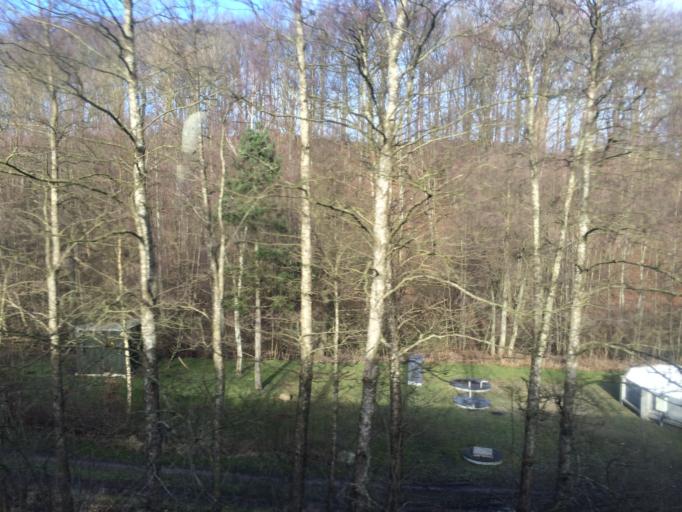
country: DK
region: South Denmark
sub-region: Vejle Kommune
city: Jelling
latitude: 55.7665
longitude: 9.4691
